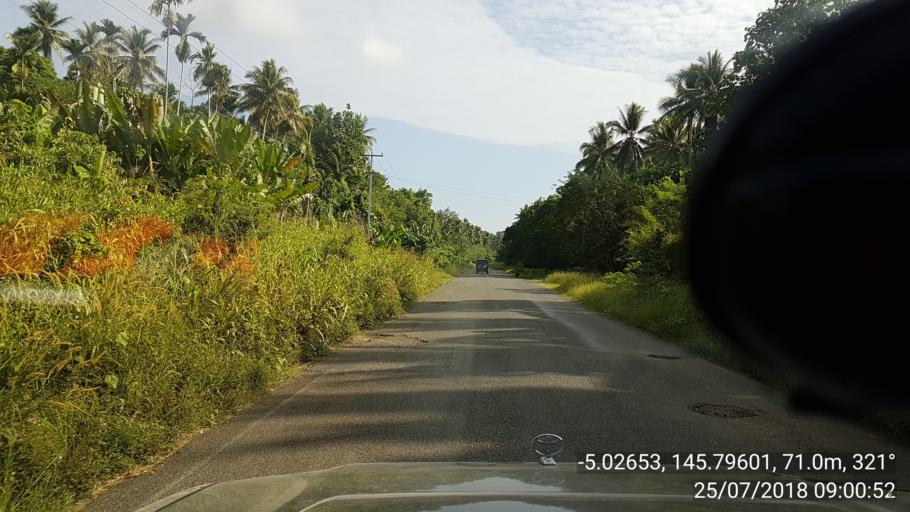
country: PG
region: Madang
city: Madang
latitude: -5.0265
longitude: 145.7962
